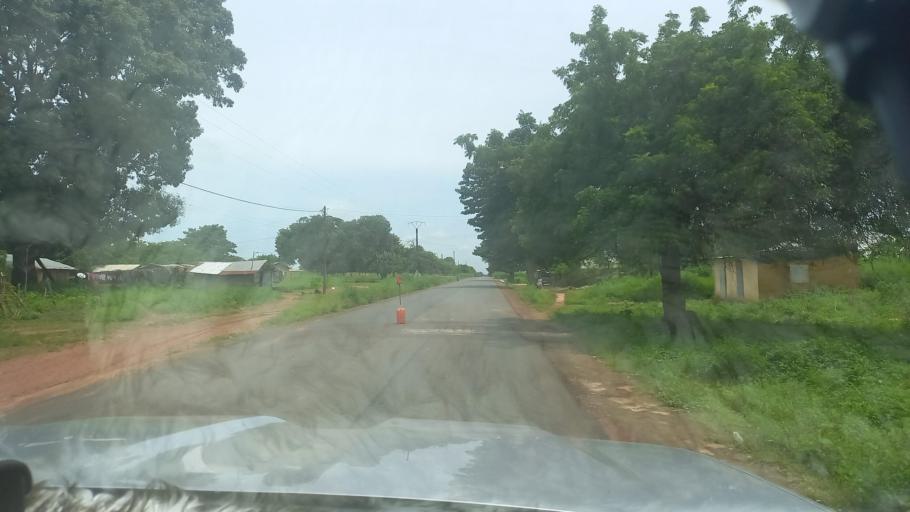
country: SN
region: Kolda
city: Marsassoum
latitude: 12.9620
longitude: -15.9850
